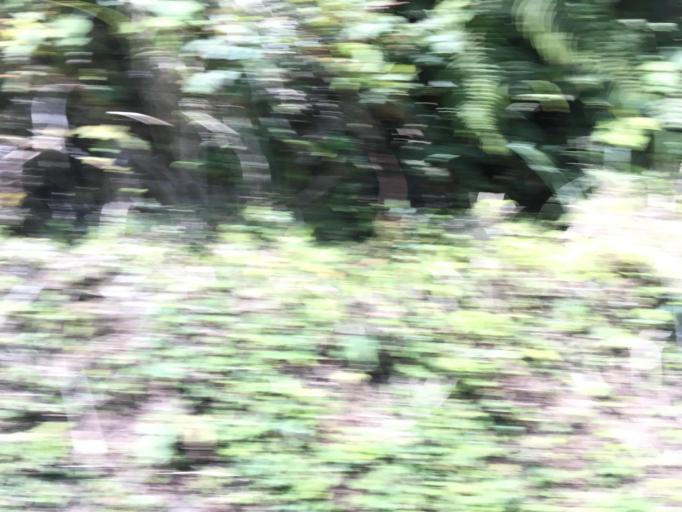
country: TW
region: Taiwan
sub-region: Yilan
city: Yilan
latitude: 24.5200
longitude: 121.5218
